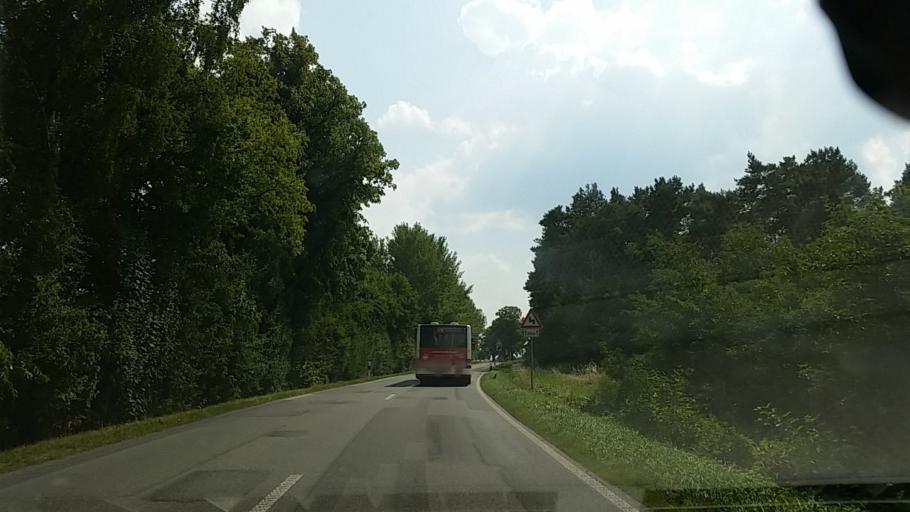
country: DE
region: Schleswig-Holstein
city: Schmilau
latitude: 53.6768
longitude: 10.7714
